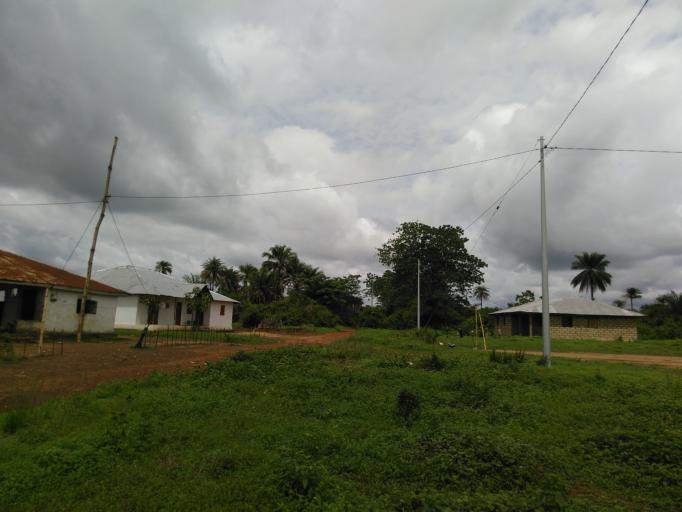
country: SL
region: Northern Province
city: Rokupr
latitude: 8.6448
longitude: -12.4493
